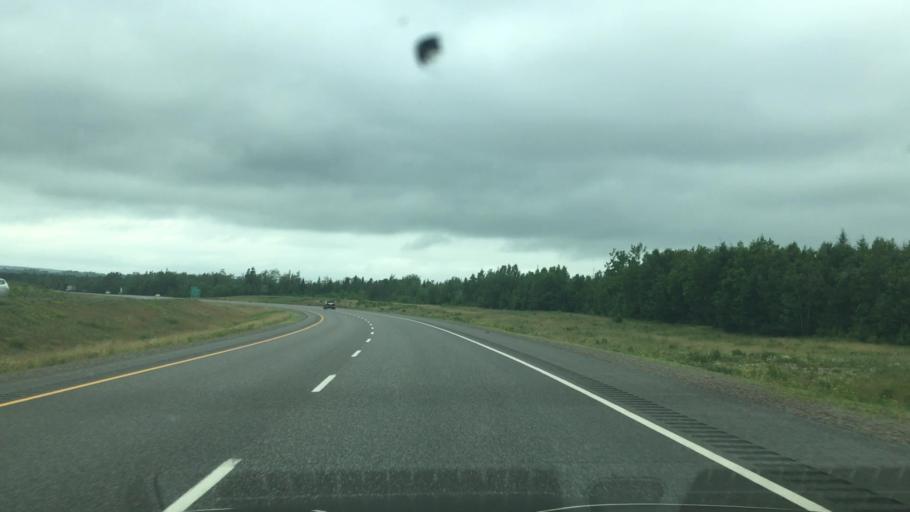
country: CA
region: Nova Scotia
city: Truro
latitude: 45.4301
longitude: -63.5532
